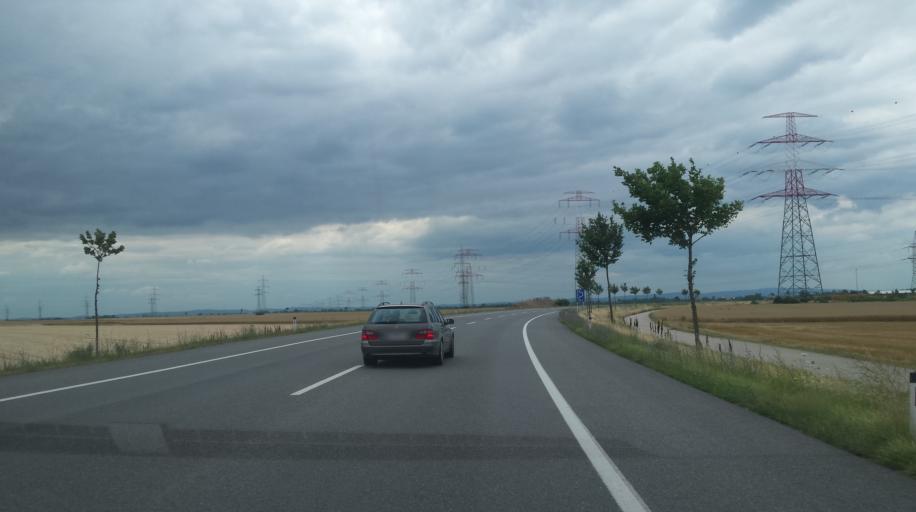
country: AT
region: Lower Austria
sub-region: Politischer Bezirk Wien-Umgebung
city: Himberg
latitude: 48.0791
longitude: 16.4608
